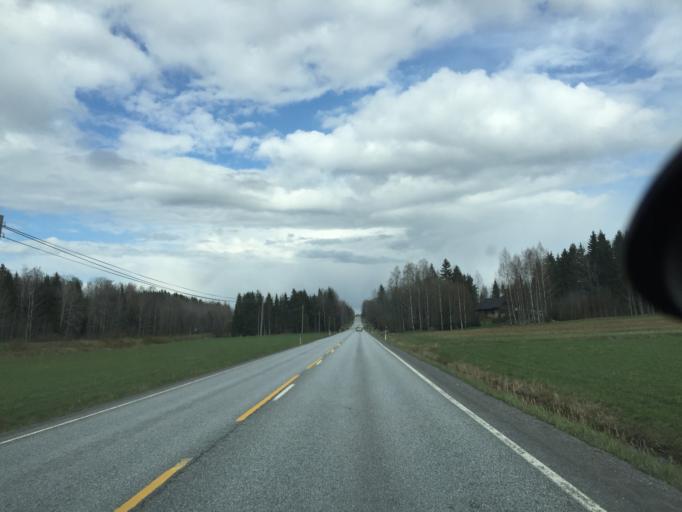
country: FI
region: Uusimaa
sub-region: Raaseporin
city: Inga
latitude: 60.1624
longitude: 23.9378
